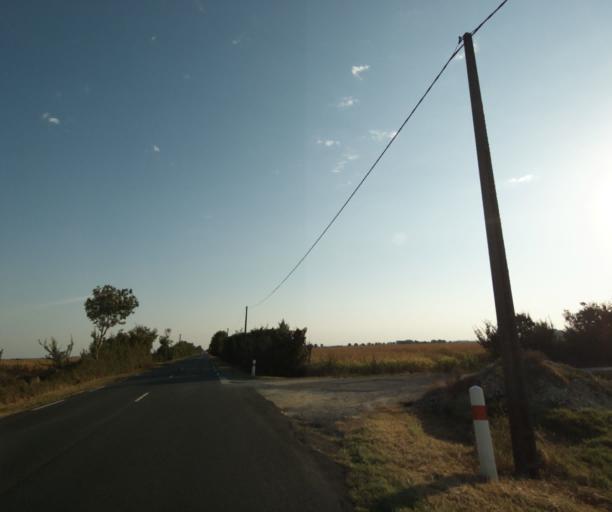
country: FR
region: Poitou-Charentes
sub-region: Departement de la Charente-Maritime
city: Tonnay-Charente
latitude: 45.9729
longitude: -0.9164
